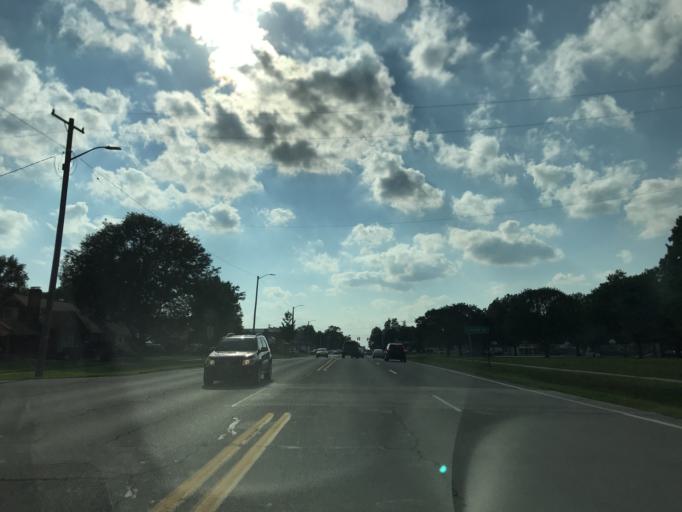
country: US
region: Michigan
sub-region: Wayne County
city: Redford
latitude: 42.3987
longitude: -83.3120
